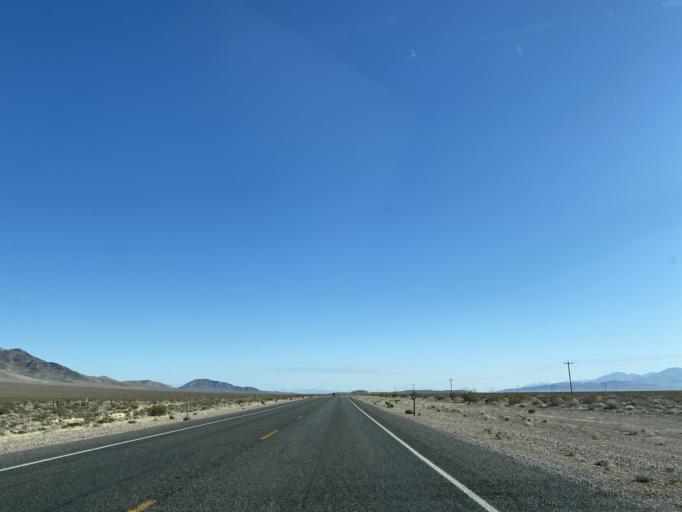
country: US
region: Nevada
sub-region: Nye County
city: Beatty
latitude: 36.8019
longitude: -116.7179
